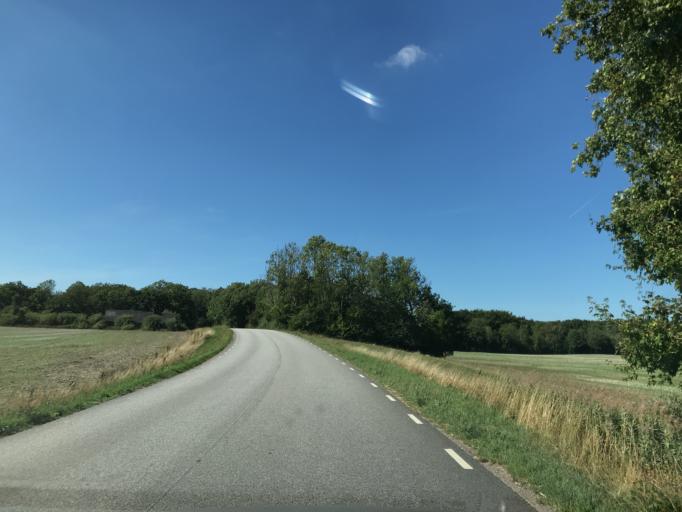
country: SE
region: Skane
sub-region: Tomelilla Kommun
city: Tomelilla
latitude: 55.6533
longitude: 13.9418
